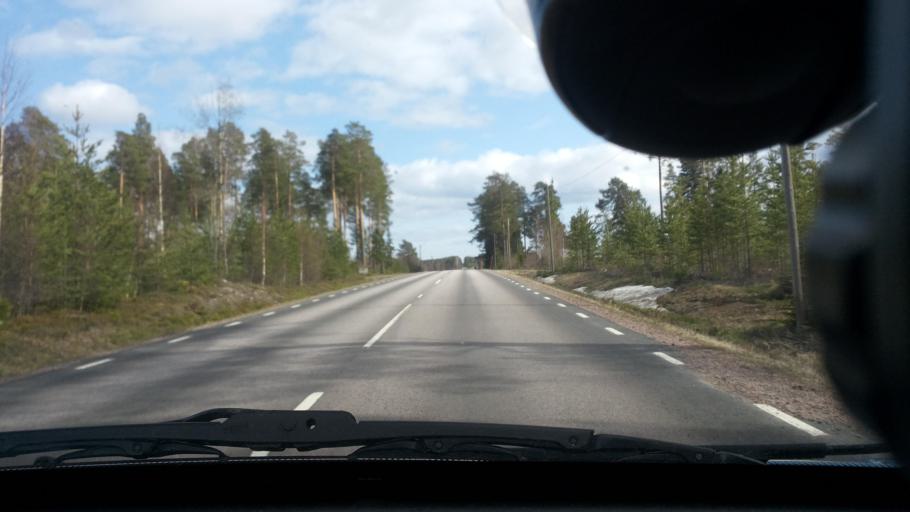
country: SE
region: Norrbotten
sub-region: Lulea Kommun
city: Sodra Sunderbyn
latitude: 65.6428
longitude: 21.8926
